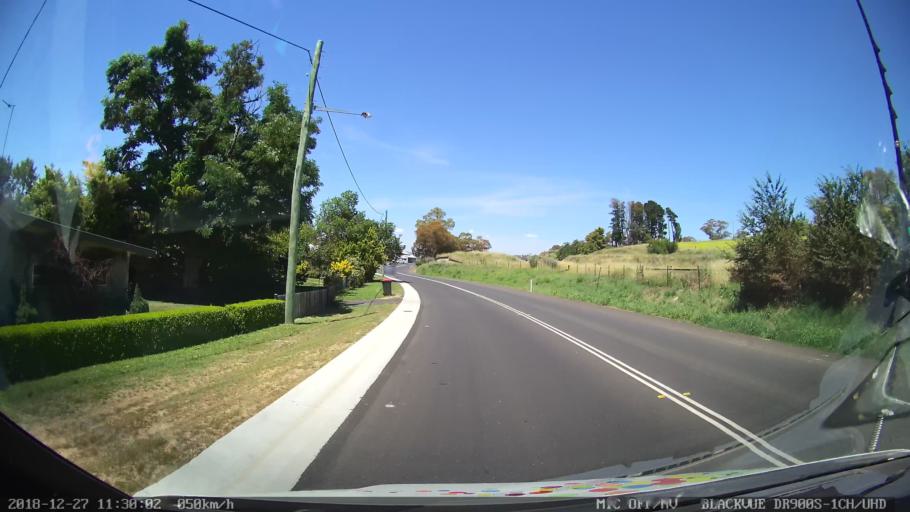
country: AU
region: New South Wales
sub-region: Bathurst Regional
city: Perthville
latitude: -33.4849
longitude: 149.5478
